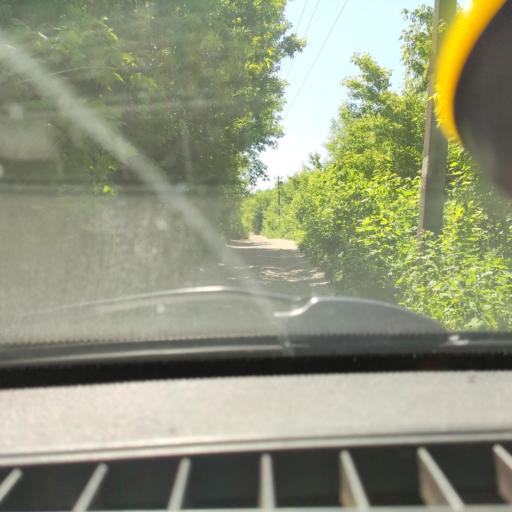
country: RU
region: Samara
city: Zhigulevsk
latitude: 53.3765
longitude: 49.5092
